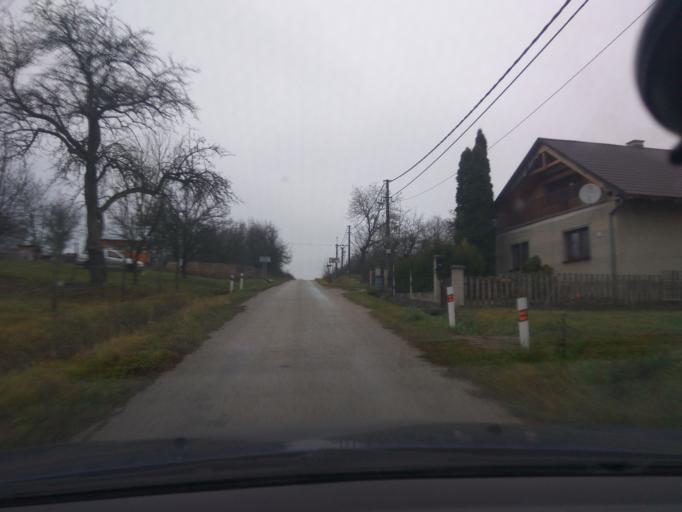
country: SK
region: Trnavsky
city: Vrbove
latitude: 48.6754
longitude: 17.6820
